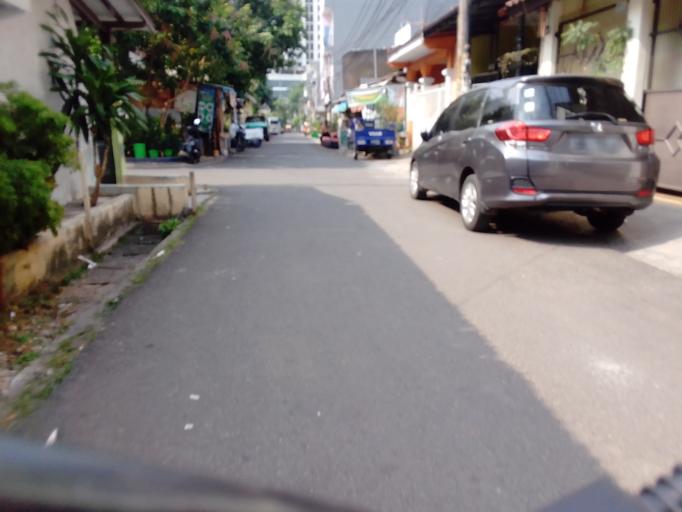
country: ID
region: Jakarta Raya
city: Jakarta
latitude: -6.2042
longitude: 106.8063
